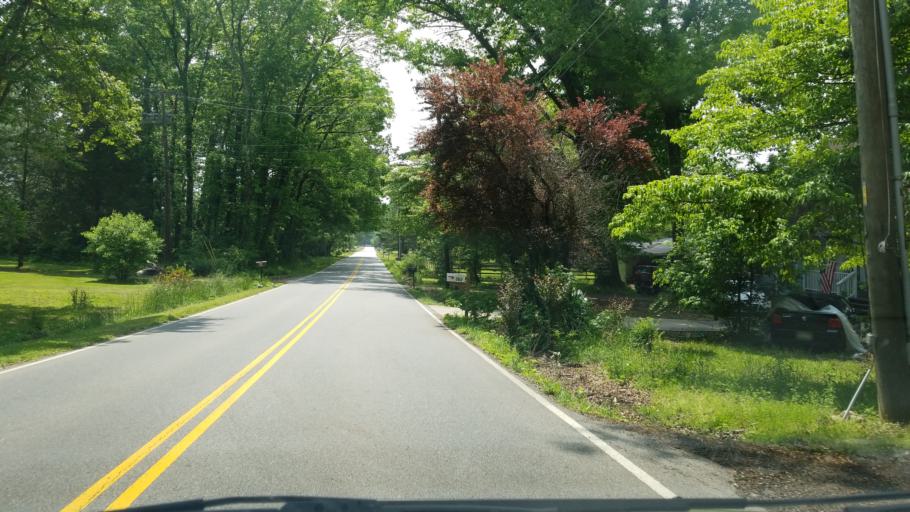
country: US
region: Tennessee
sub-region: Hamilton County
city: Falling Water
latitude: 35.2319
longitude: -85.2298
